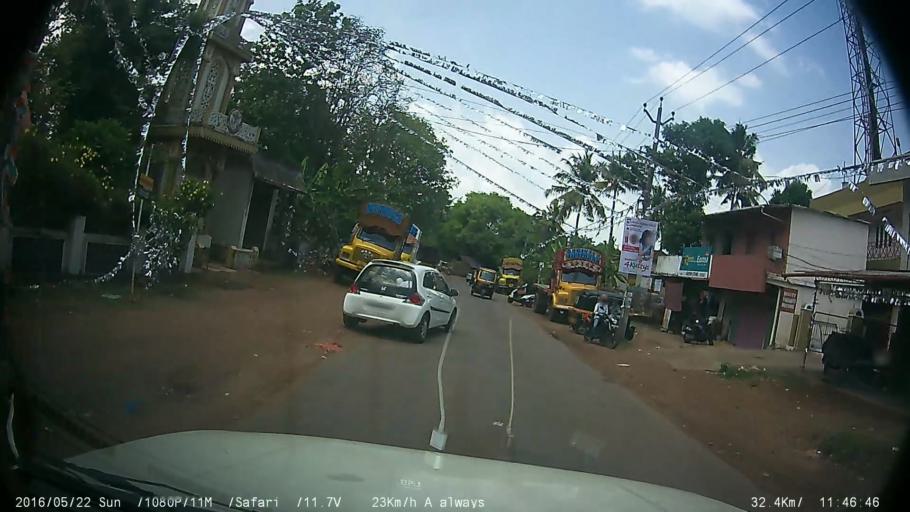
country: IN
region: Kerala
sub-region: Kottayam
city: Kottayam
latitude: 9.5327
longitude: 76.5230
